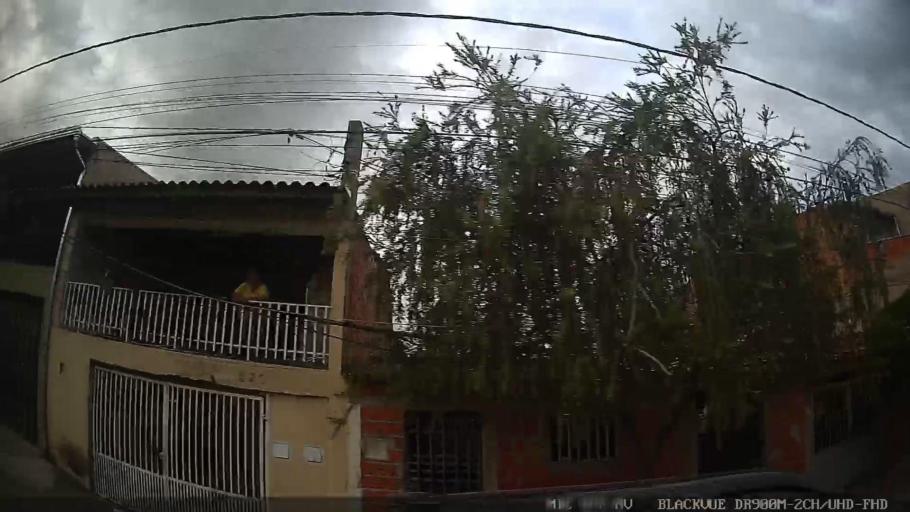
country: BR
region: Sao Paulo
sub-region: Indaiatuba
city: Indaiatuba
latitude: -23.1303
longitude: -47.2410
